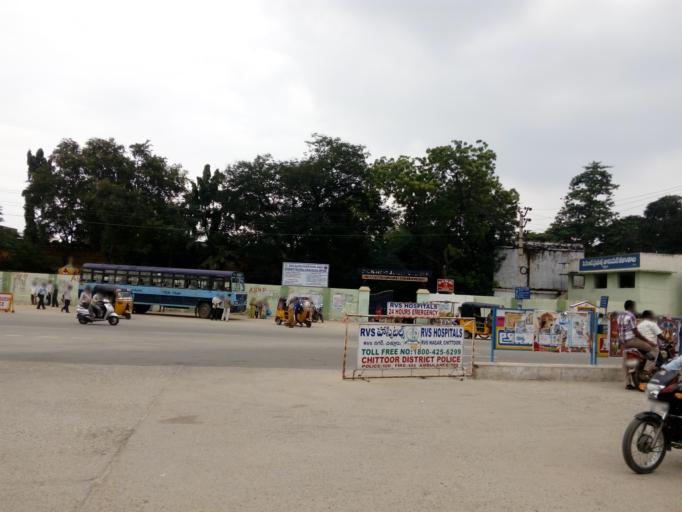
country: IN
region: Andhra Pradesh
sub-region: Chittoor
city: Chittoor
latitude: 13.2168
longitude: 79.1019
